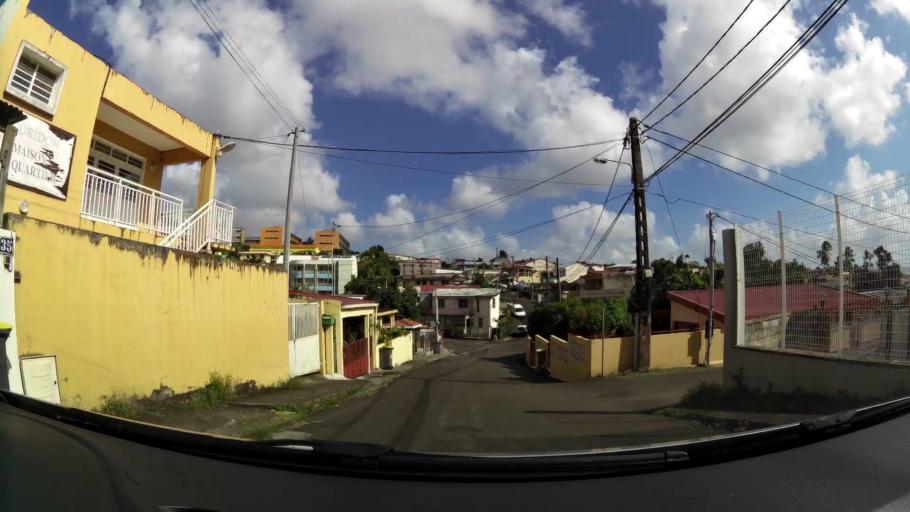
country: MQ
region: Martinique
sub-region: Martinique
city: Fort-de-France
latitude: 14.6228
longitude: -61.0584
